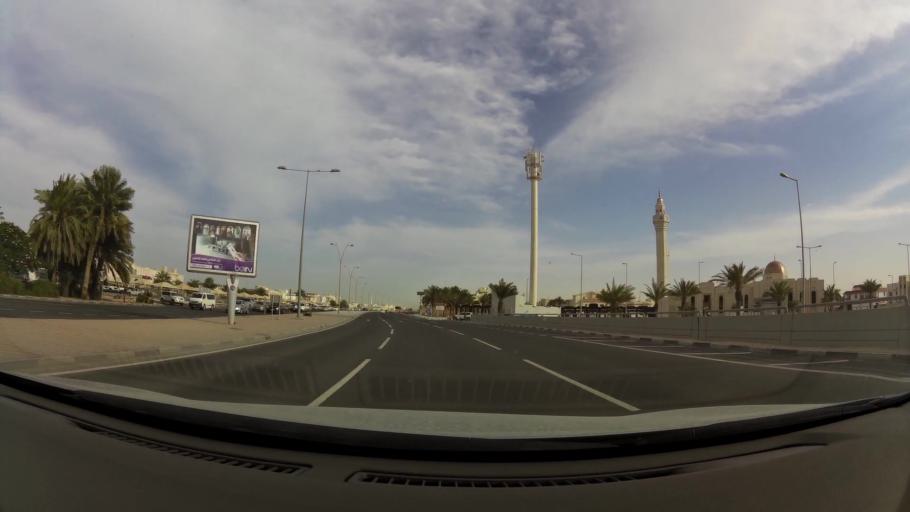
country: QA
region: Baladiyat ad Dawhah
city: Doha
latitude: 25.2516
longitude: 51.5368
